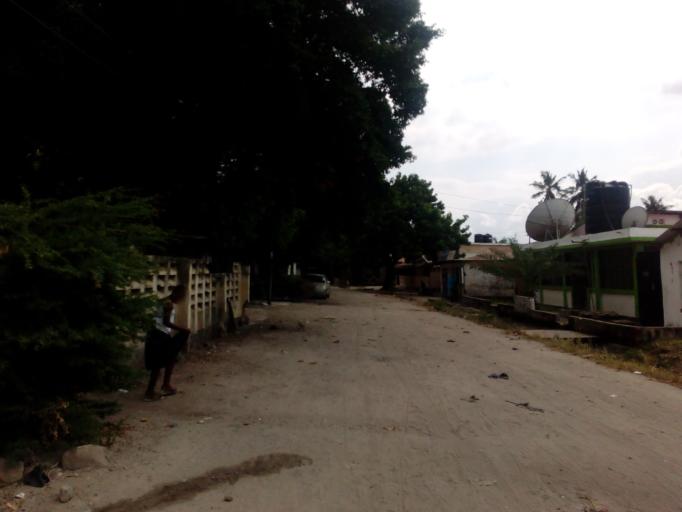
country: TZ
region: Dar es Salaam
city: Dar es Salaam
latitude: -6.8524
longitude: 39.2591
